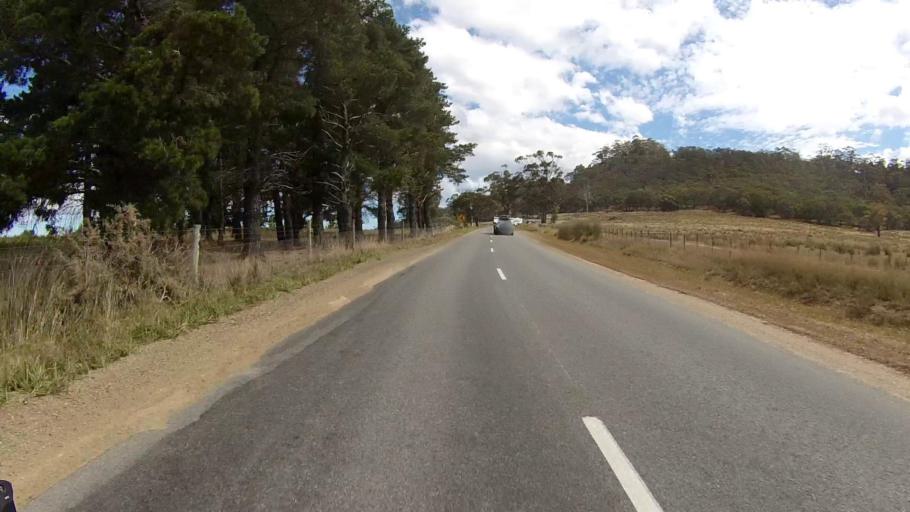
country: AU
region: Tasmania
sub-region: Break O'Day
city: St Helens
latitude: -41.9686
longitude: 148.1524
